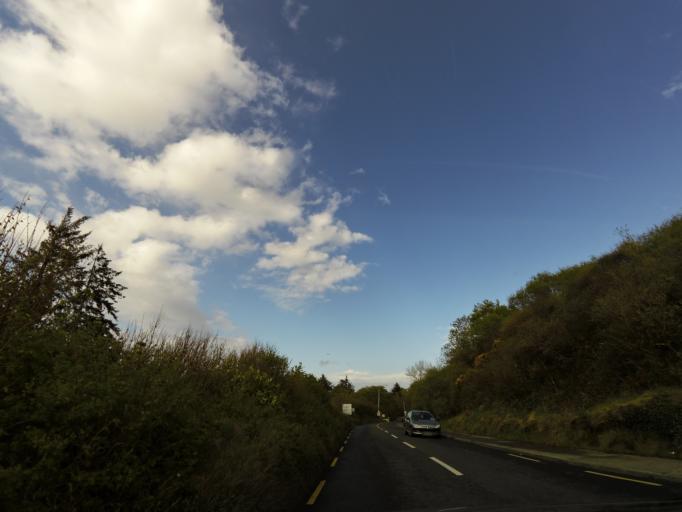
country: IE
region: Connaught
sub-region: County Galway
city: Bearna
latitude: 53.0245
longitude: -9.2916
